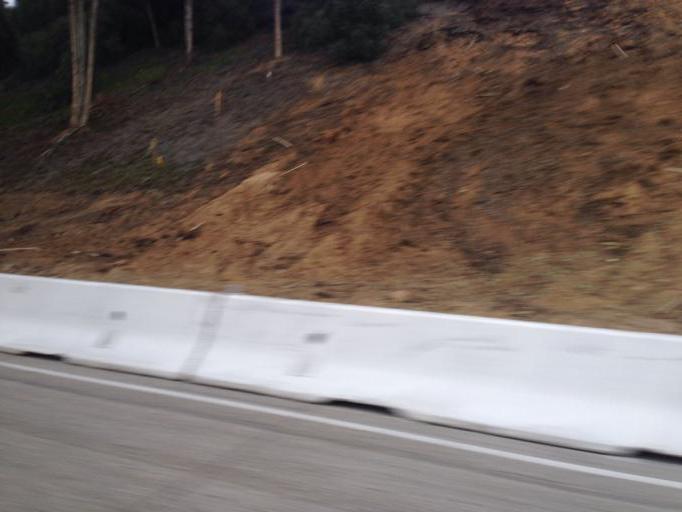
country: US
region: California
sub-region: San Diego County
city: National City
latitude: 32.6686
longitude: -117.0808
